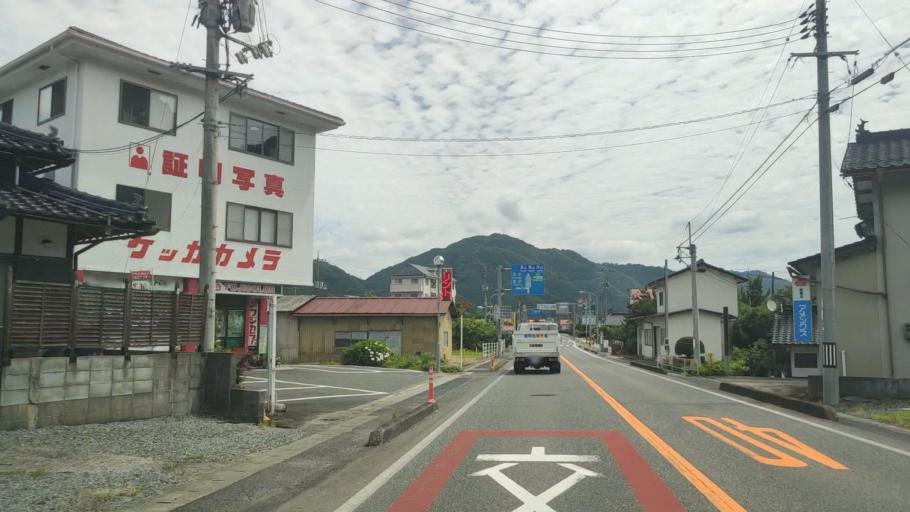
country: JP
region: Okayama
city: Niimi
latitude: 35.0778
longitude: 133.6893
